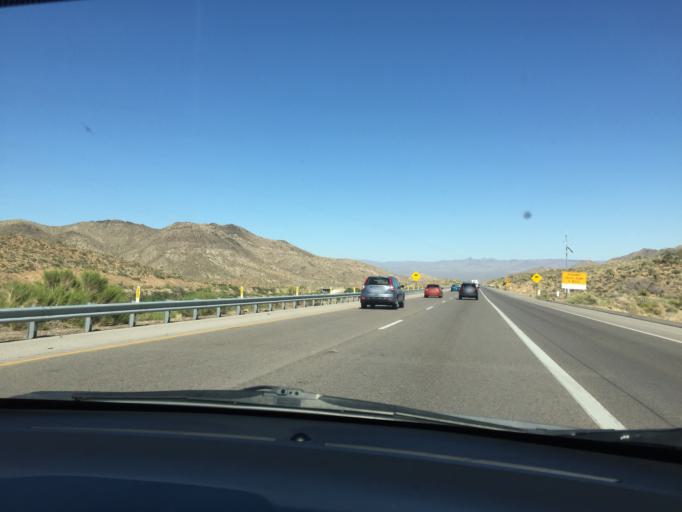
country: US
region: Nevada
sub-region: Clark County
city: Sandy Valley
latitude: 35.4681
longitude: -115.4953
